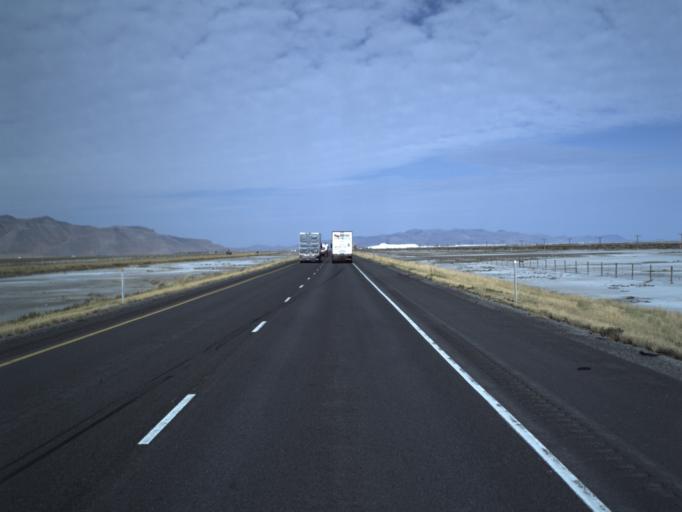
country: US
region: Utah
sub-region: Tooele County
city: Grantsville
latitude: 40.6962
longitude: -112.4754
